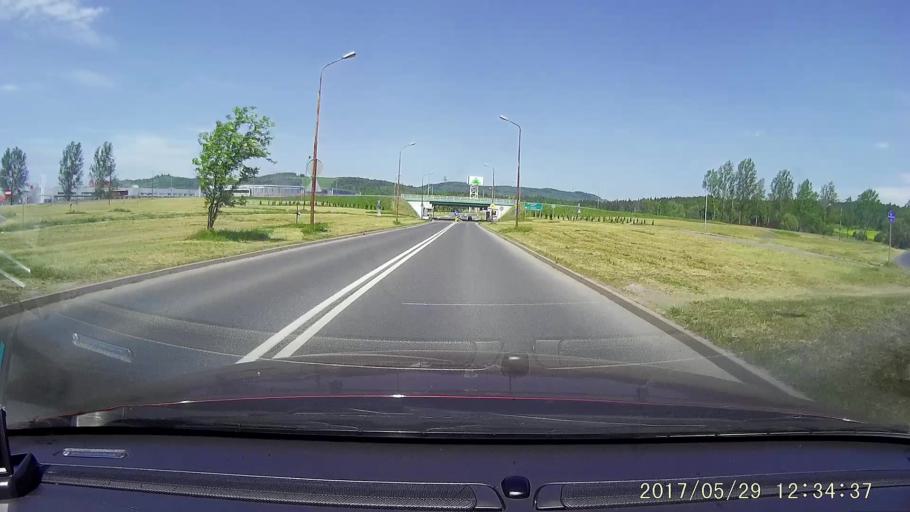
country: PL
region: Lower Silesian Voivodeship
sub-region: Powiat jeleniogorski
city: Jezow Sudecki
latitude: 50.9186
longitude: 15.7640
